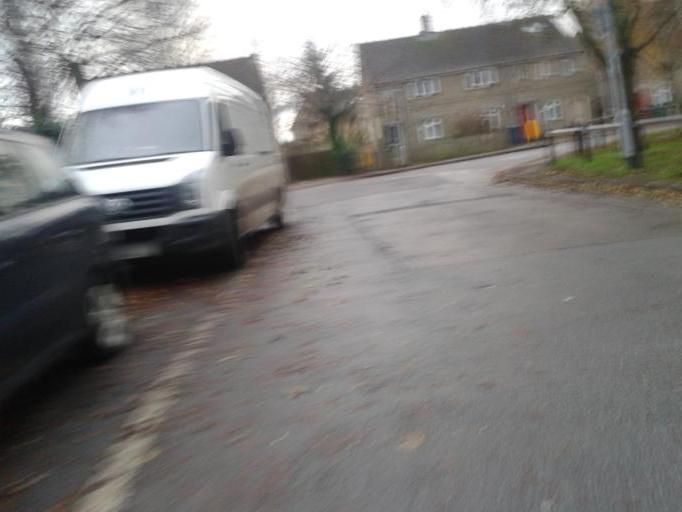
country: GB
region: England
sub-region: Cambridgeshire
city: Cambridge
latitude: 52.2086
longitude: 0.1420
